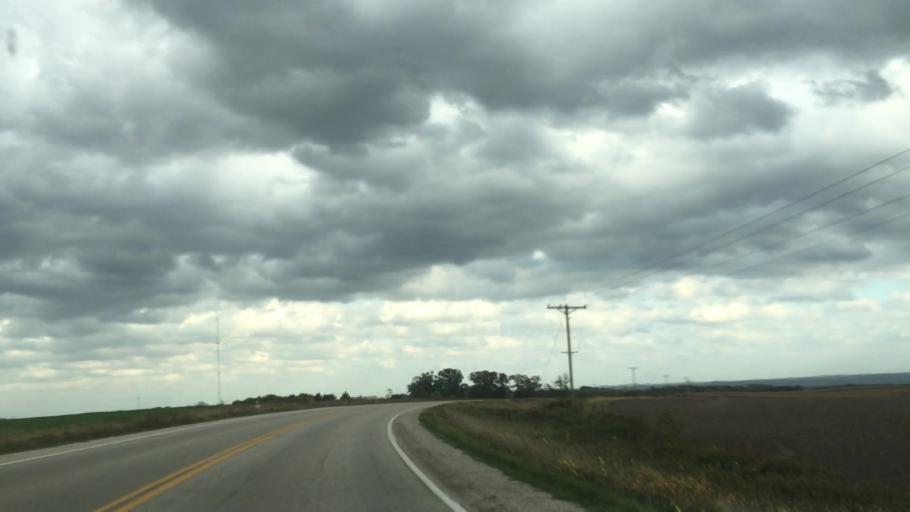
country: US
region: Minnesota
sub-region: Fillmore County
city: Preston
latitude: 43.7349
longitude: -92.1000
